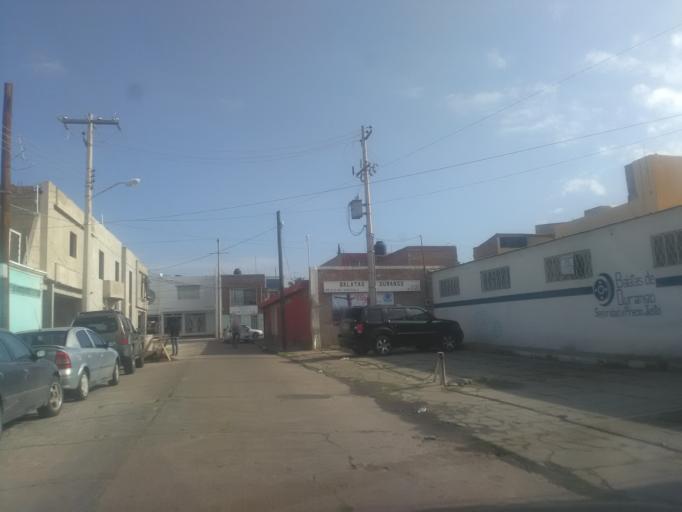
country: MX
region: Durango
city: Victoria de Durango
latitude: 24.0275
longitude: -104.6598
